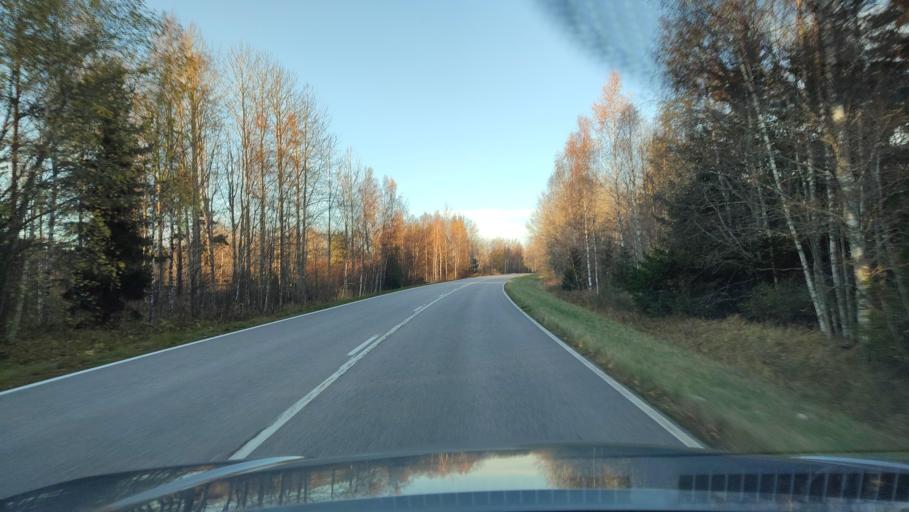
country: FI
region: Ostrobothnia
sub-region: Sydosterbotten
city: Kristinestad
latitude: 62.2873
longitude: 21.3775
